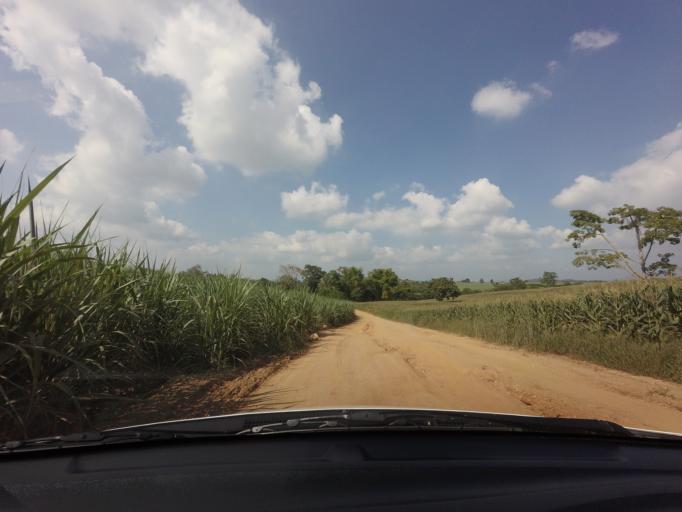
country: TH
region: Nakhon Ratchasima
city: Wang Nam Khiao
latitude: 14.4978
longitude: 101.6309
